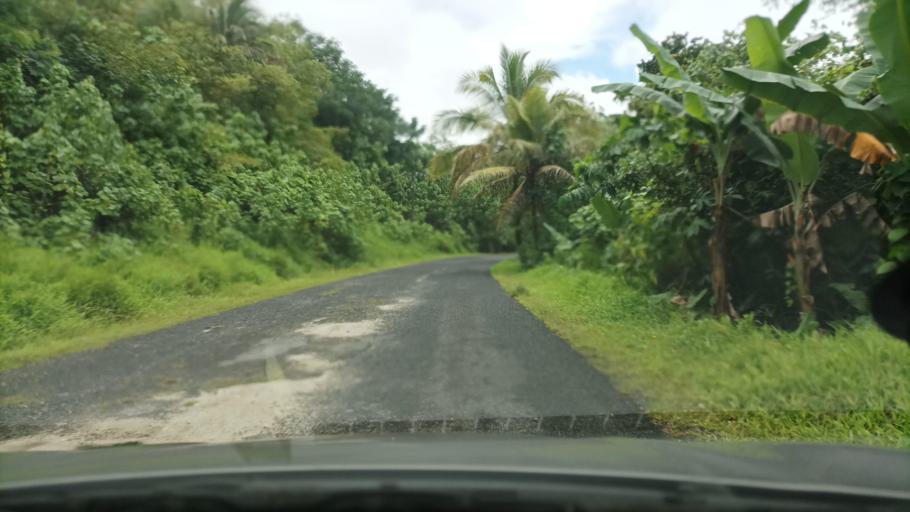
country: FM
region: Pohnpei
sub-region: Madolenihm Municipality
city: Madolenihm Municipality Government
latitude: 6.8578
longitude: 158.2921
